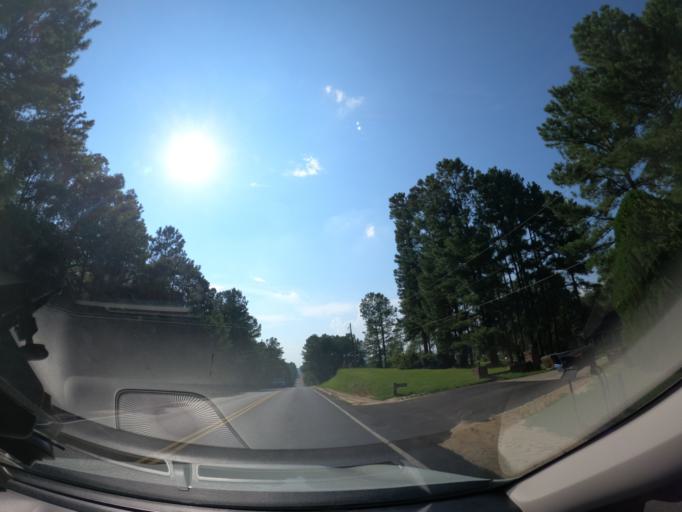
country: US
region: South Carolina
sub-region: Aiken County
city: Jackson
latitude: 33.4014
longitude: -81.7646
